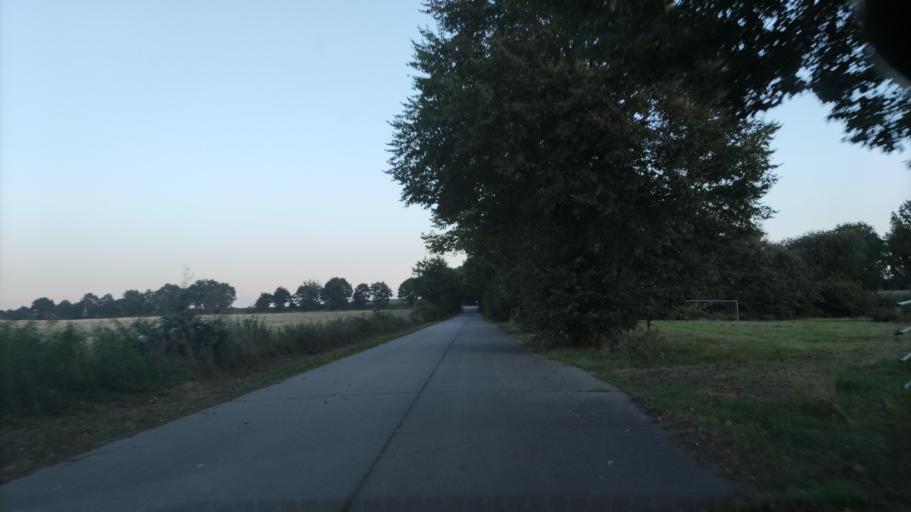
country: DE
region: Lower Saxony
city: Bispingen
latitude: 53.1273
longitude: 10.0066
